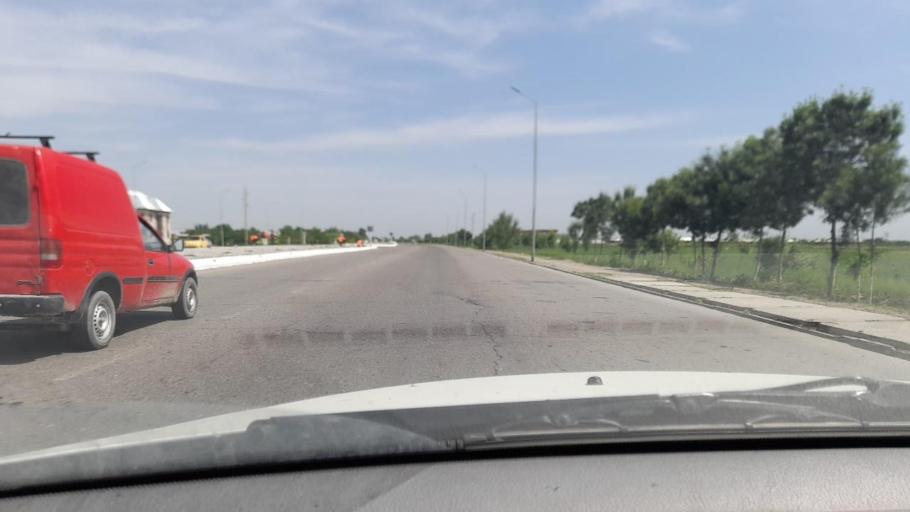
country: UZ
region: Bukhara
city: Galaosiyo
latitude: 39.8676
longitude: 64.4514
